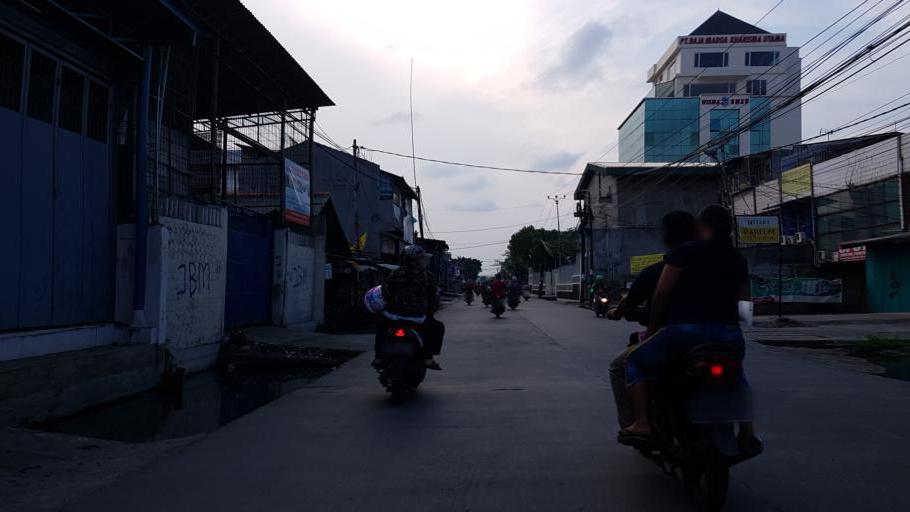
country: ID
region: Jakarta Raya
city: Jakarta
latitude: -6.1396
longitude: 106.7648
